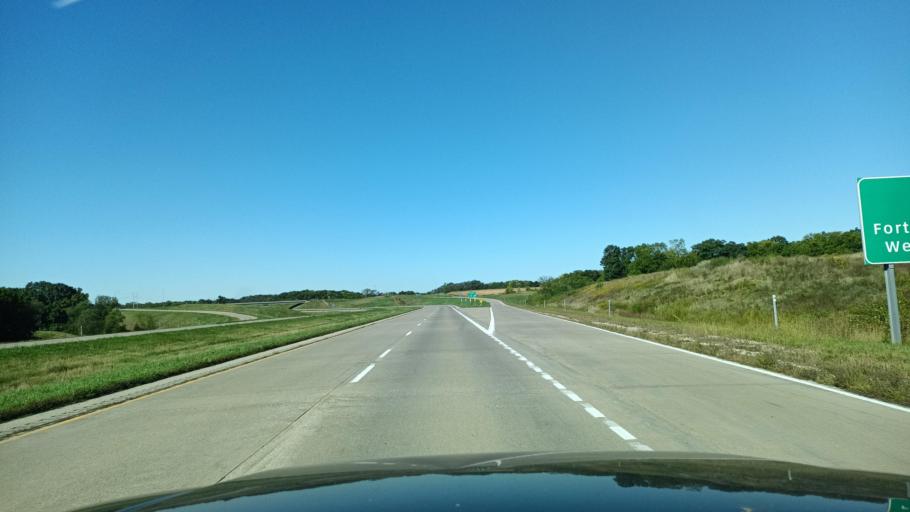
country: US
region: Iowa
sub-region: Lee County
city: Fort Madison
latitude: 40.6705
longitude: -91.3503
